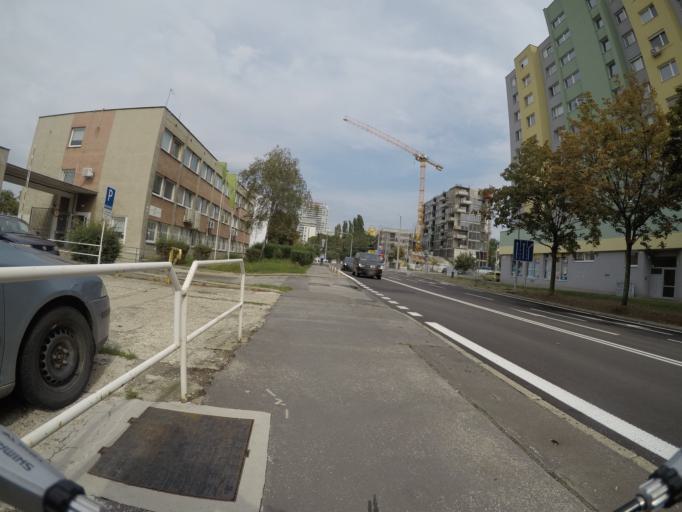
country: SK
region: Bratislavsky
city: Bratislava
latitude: 48.1484
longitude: 17.1579
